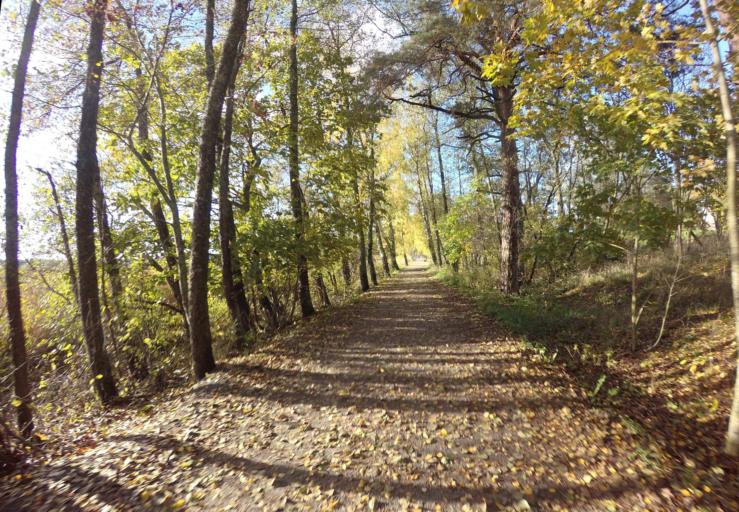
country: FI
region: Varsinais-Suomi
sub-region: Turku
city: Raisio
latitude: 60.4330
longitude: 22.1939
